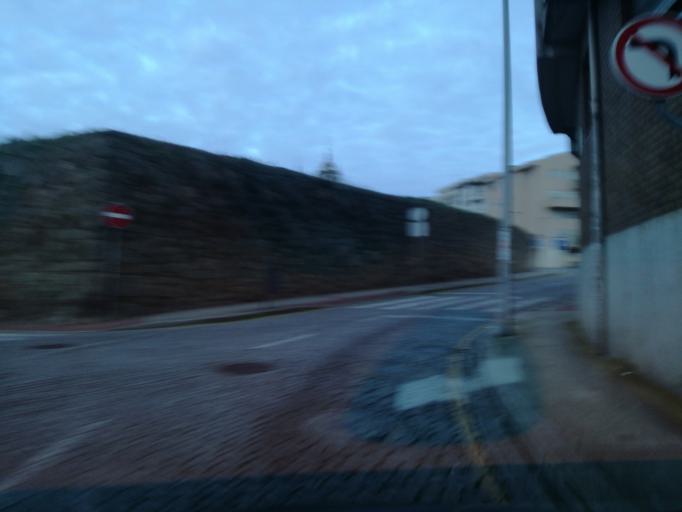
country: PT
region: Porto
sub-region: Vila Nova de Gaia
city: Canidelo
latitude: 41.1523
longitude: -8.6491
